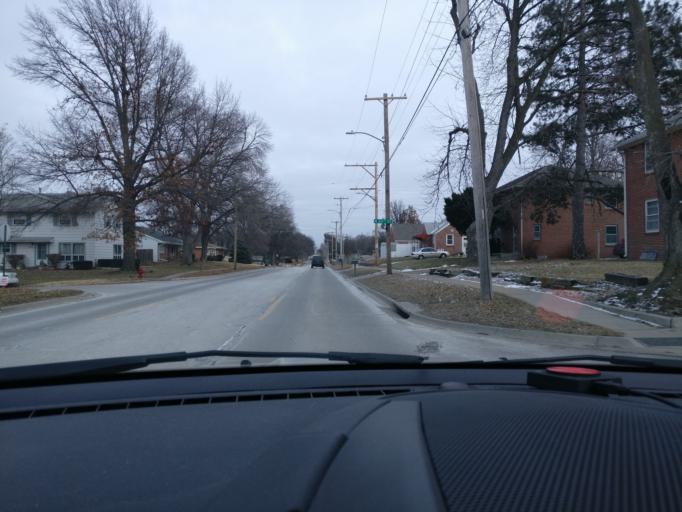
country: US
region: Nebraska
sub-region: Lancaster County
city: Lincoln
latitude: 40.8425
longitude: -96.6389
